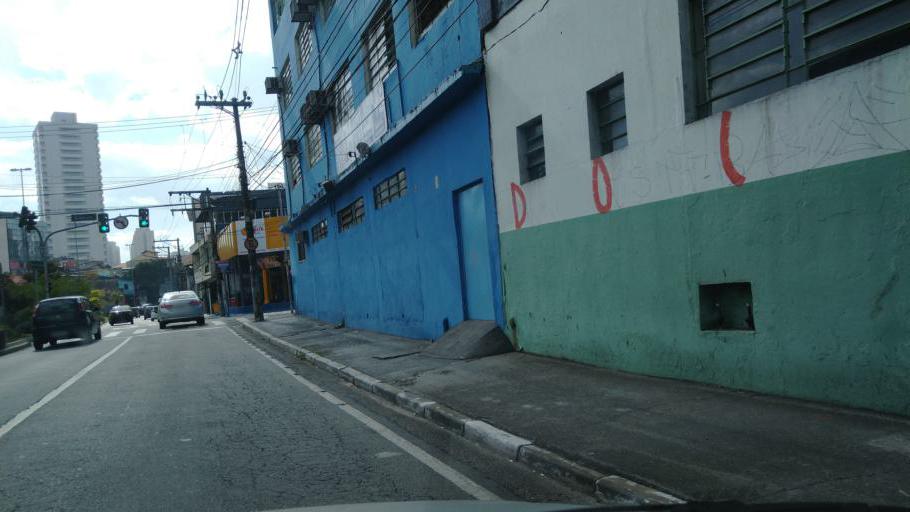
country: BR
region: Sao Paulo
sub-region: Guarulhos
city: Guarulhos
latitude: -23.4685
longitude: -46.5350
